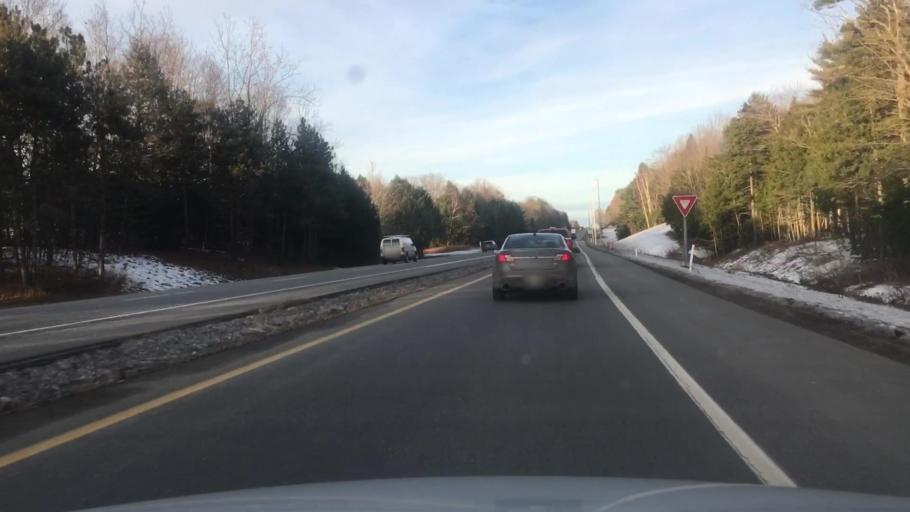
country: US
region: Maine
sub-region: Kennebec County
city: Augusta
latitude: 44.3560
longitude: -69.7806
